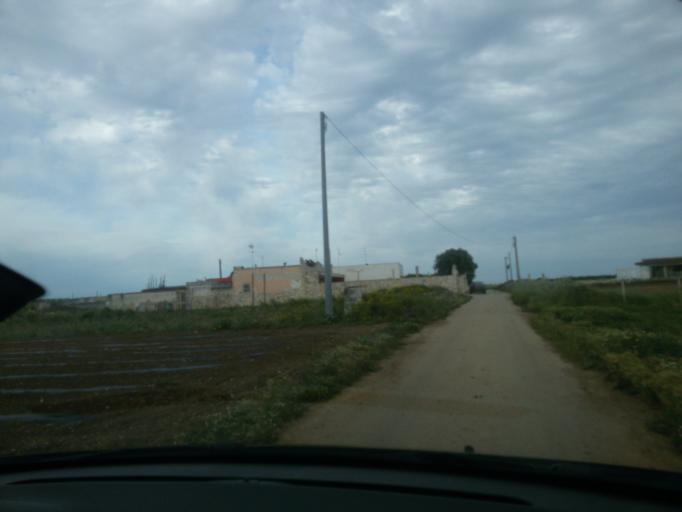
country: IT
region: Apulia
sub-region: Provincia di Brindisi
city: Brindisi
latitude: 40.6549
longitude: 17.8678
